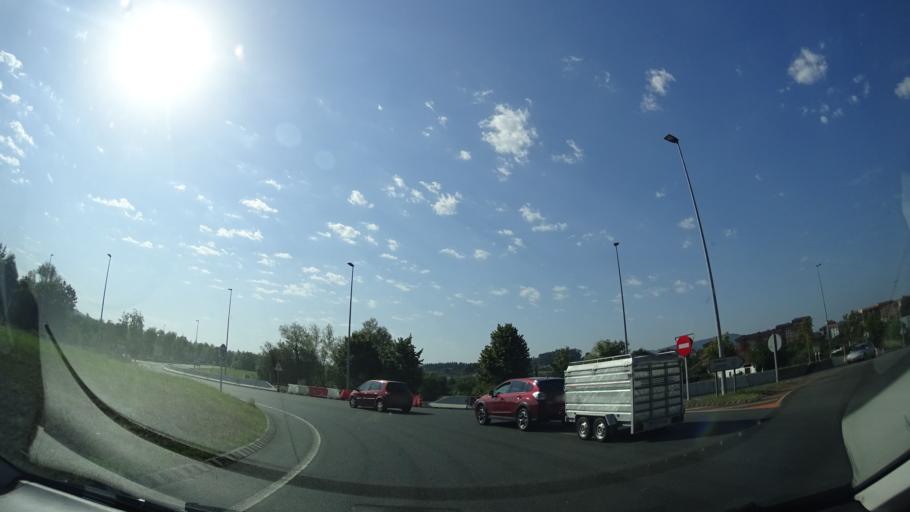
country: ES
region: Basque Country
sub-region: Bizkaia
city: Mungia
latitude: 43.3570
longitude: -2.8376
